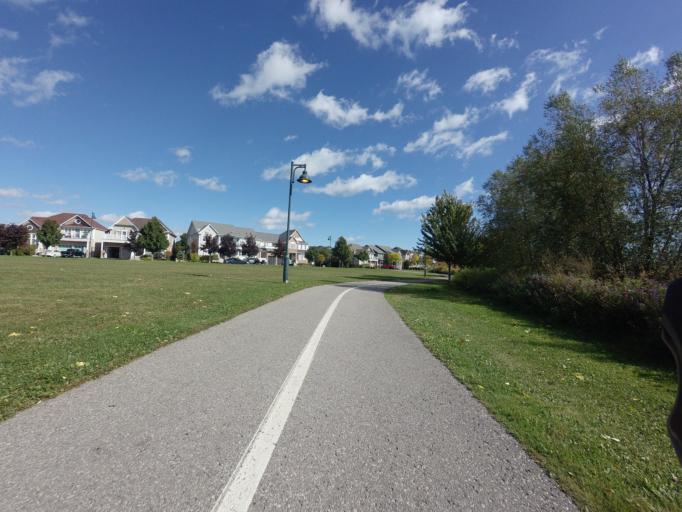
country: CA
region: Ontario
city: Ajax
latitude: 43.8309
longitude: -78.9853
